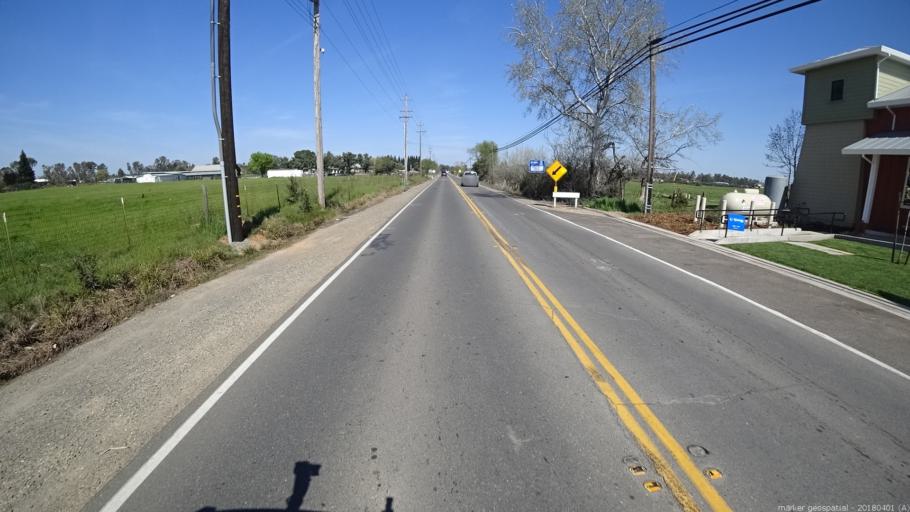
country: US
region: California
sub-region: Sacramento County
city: Wilton
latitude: 38.4018
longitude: -121.2562
